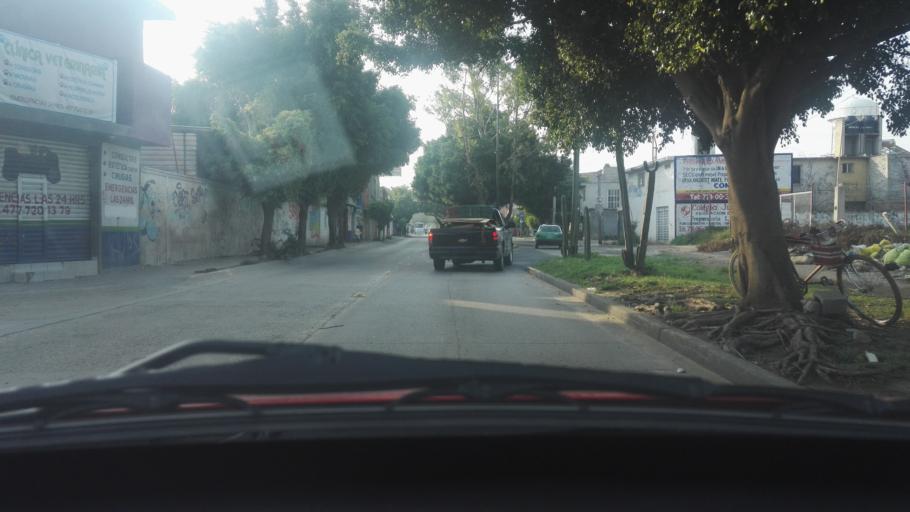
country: MX
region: Guanajuato
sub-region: Leon
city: Fraccionamiento Paraiso Real
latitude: 21.0992
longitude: -101.6081
